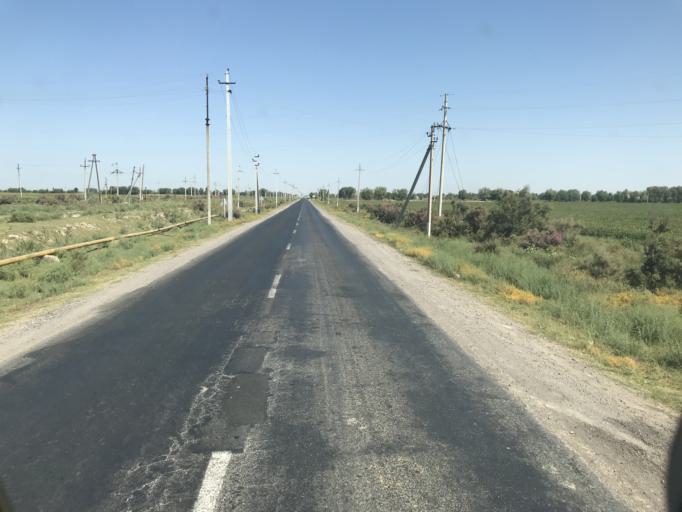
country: KZ
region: Ongtustik Qazaqstan
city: Ilyich
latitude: 40.8793
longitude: 68.4881
